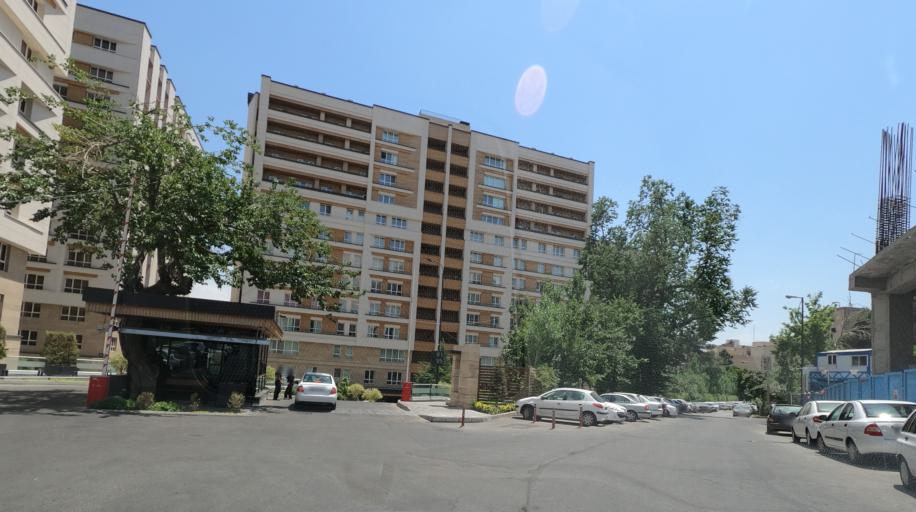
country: IR
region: Tehran
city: Tajrish
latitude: 35.7895
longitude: 51.3855
